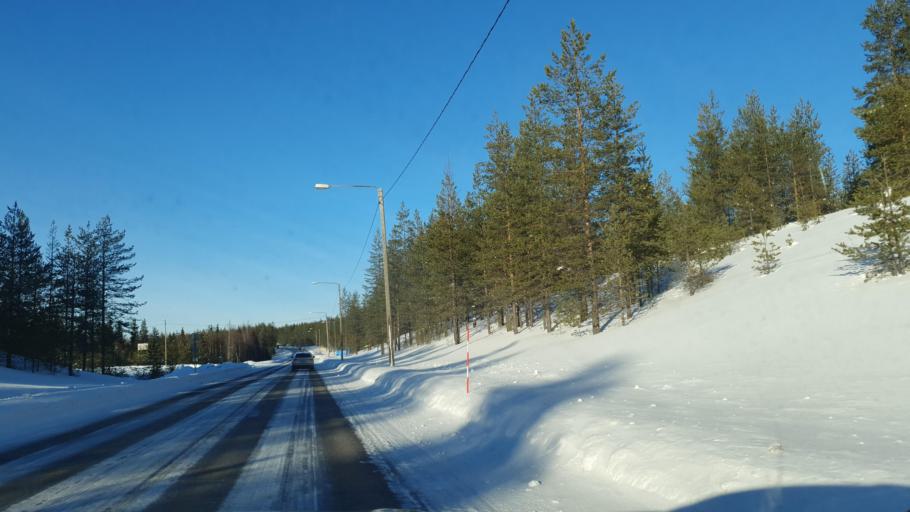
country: FI
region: Lapland
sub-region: Torniolaakso
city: Pello
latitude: 66.9143
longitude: 24.0945
